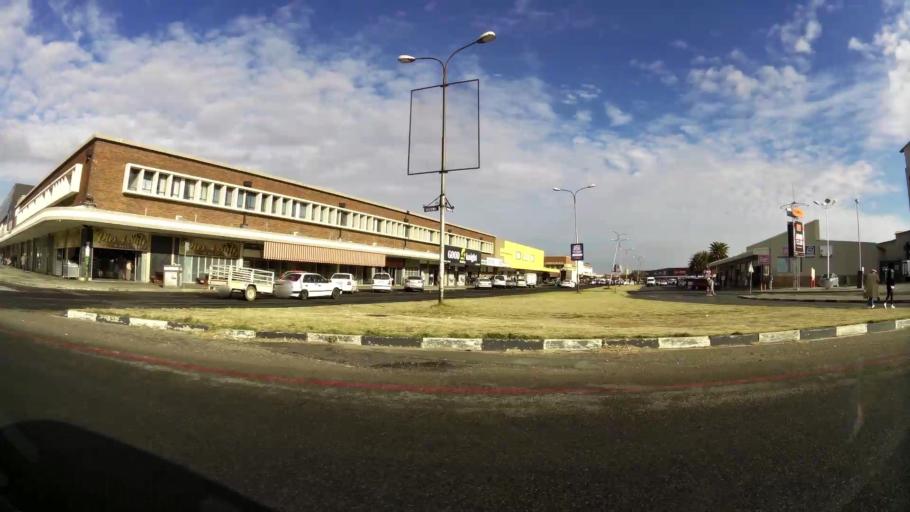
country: ZA
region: Orange Free State
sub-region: Lejweleputswa District Municipality
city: Welkom
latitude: -27.9798
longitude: 26.7357
